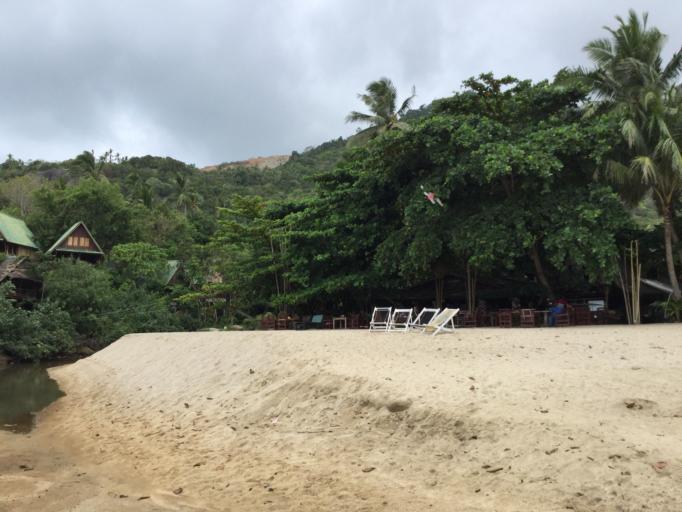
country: TH
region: Nakhon Si Thammarat
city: Ko Pha Ngan
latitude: 9.7496
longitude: 100.0745
